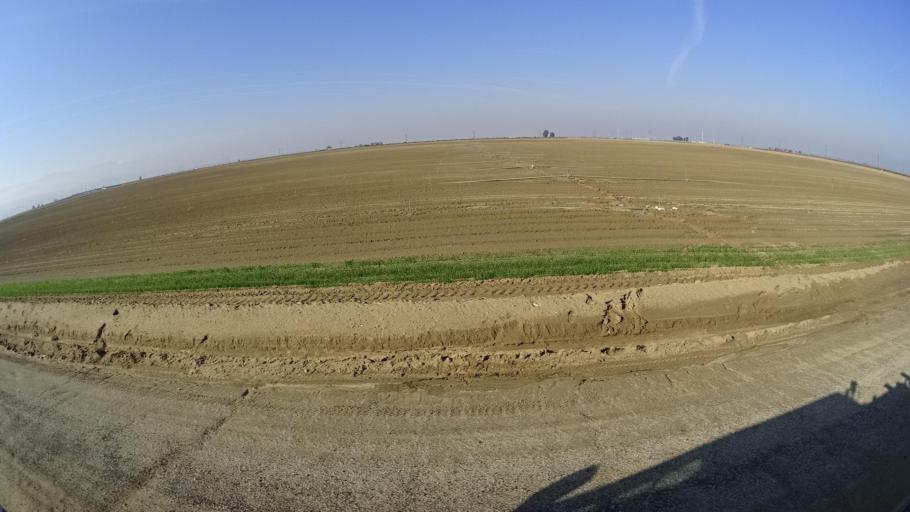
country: US
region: California
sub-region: Kern County
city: Weedpatch
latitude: 35.1054
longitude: -118.9677
